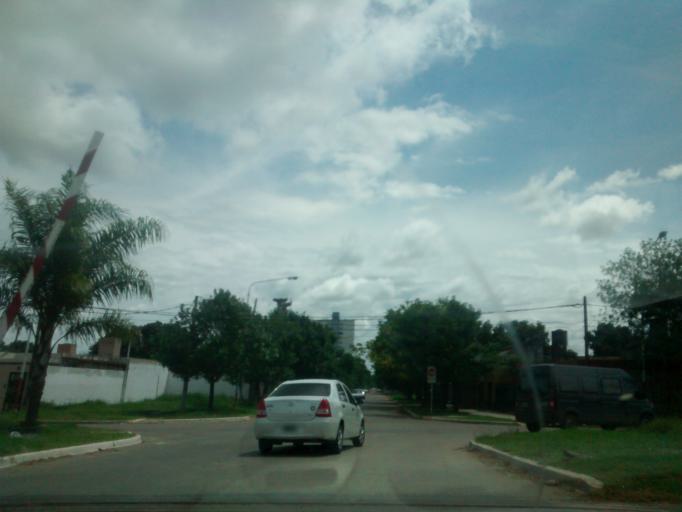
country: AR
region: Chaco
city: Resistencia
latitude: -27.4464
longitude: -59.0008
